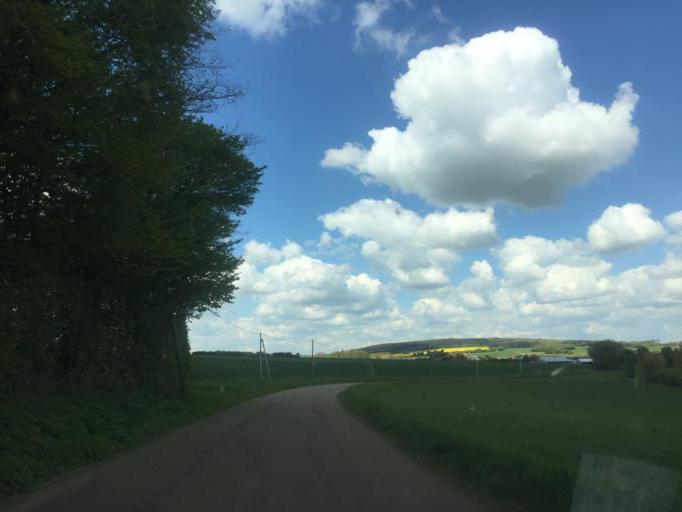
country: FR
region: Bourgogne
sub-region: Departement de l'Yonne
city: Fontenailles
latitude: 47.5524
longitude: 3.3382
